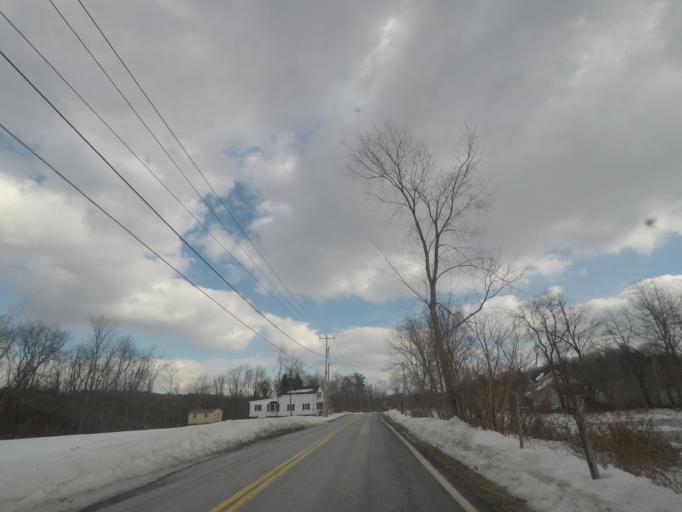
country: US
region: New York
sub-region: Saratoga County
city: Country Knolls
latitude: 42.9167
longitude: -73.7540
